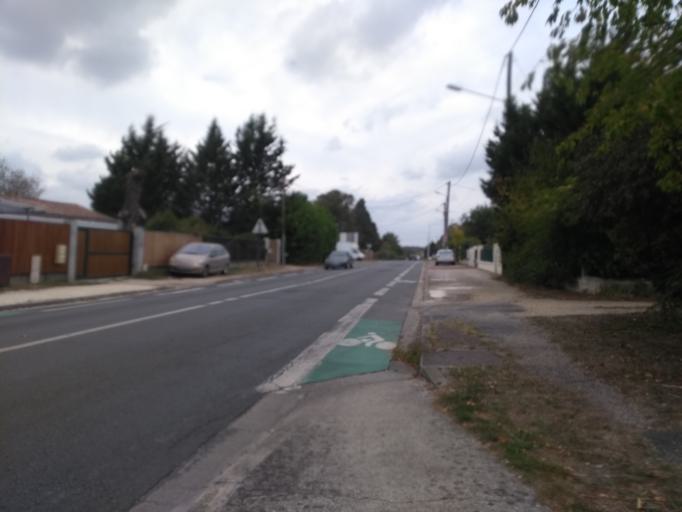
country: FR
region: Aquitaine
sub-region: Departement de la Gironde
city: Pessac
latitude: 44.8206
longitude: -0.6496
